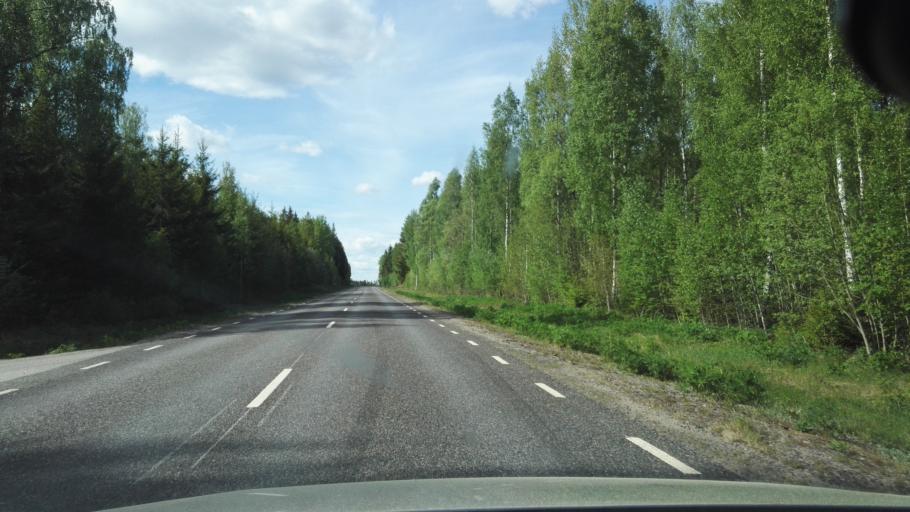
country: SE
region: Kronoberg
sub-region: Vaxjo Kommun
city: Braas
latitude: 57.0899
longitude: 14.9976
